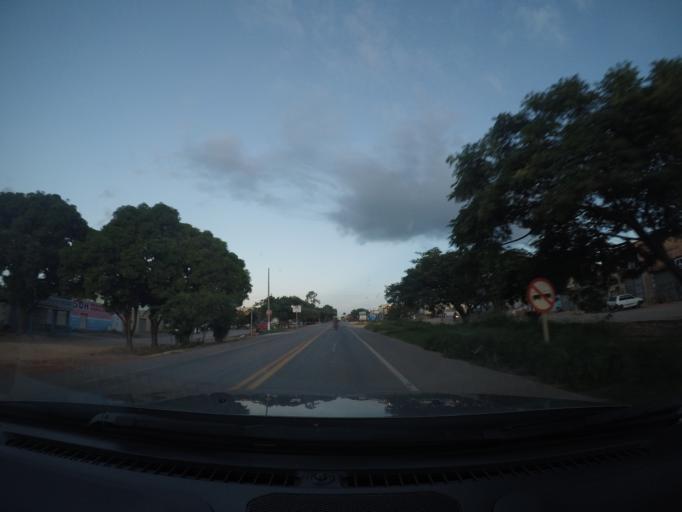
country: BR
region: Bahia
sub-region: Seabra
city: Seabra
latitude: -12.4281
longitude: -41.7749
